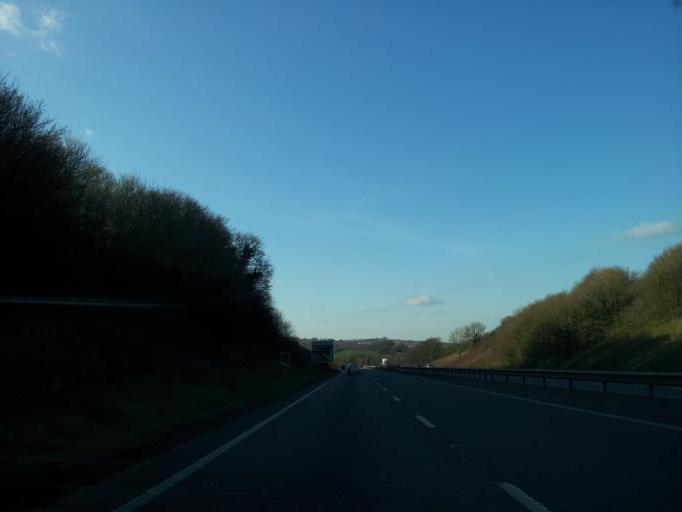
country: GB
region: England
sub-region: Devon
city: Exeter
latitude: 50.6957
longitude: -3.5409
